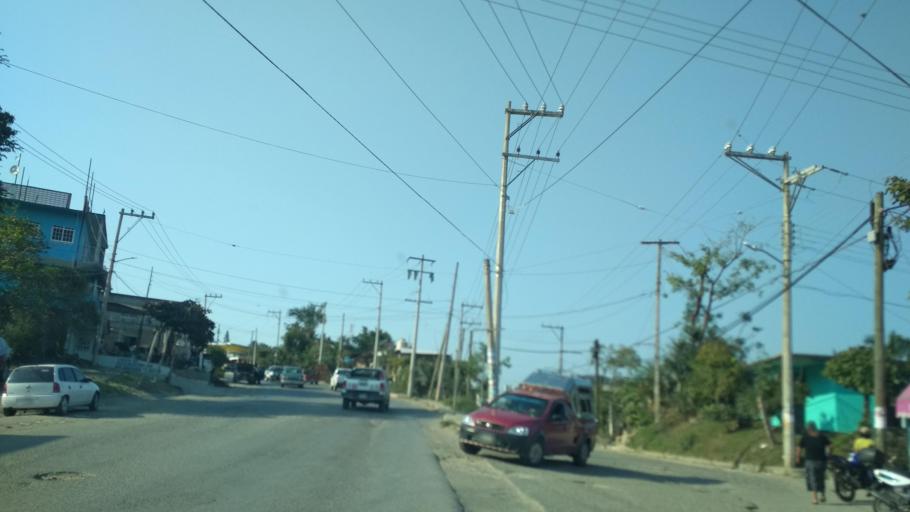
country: MM
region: Shan
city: Taunggyi
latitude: 20.4008
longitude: 97.3362
